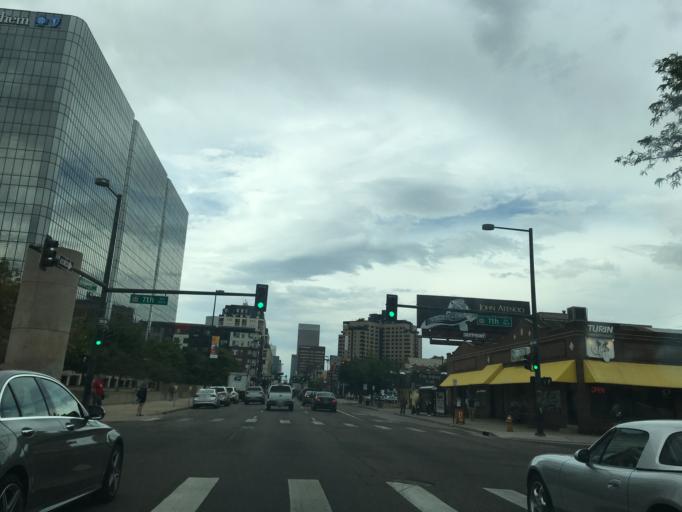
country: US
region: Colorado
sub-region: Denver County
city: Denver
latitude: 39.7270
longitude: -104.9862
